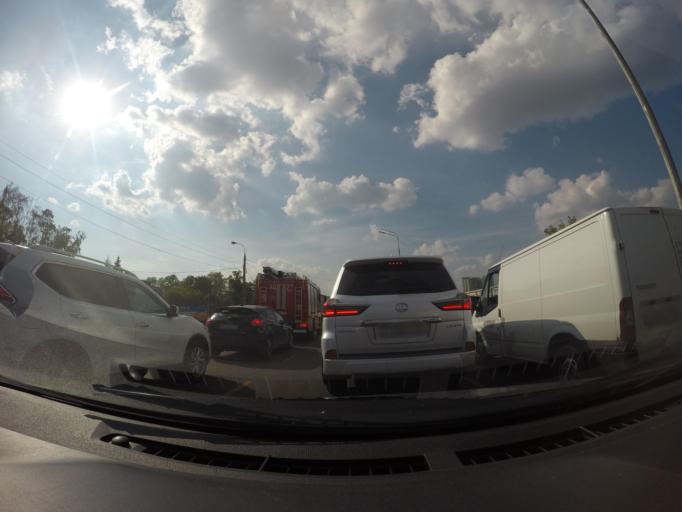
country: RU
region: Moskovskaya
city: Lyubertsy
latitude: 55.6839
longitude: 37.8835
